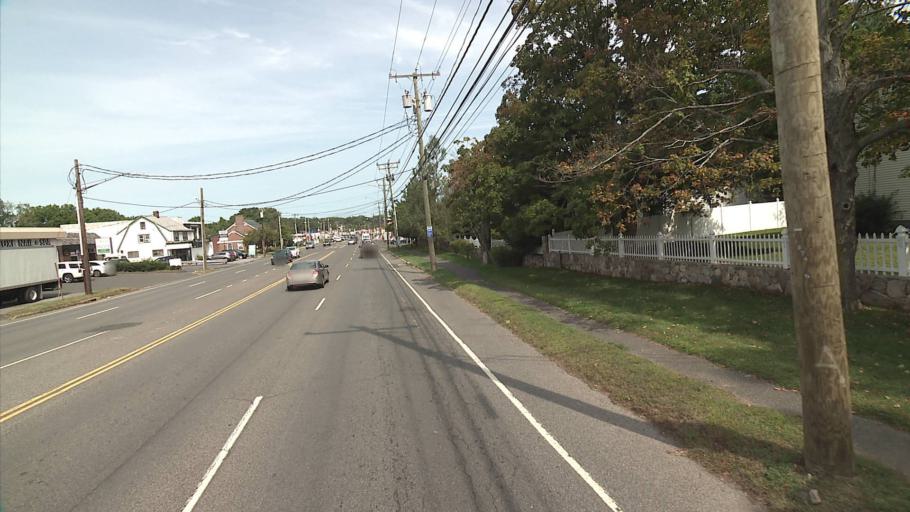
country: US
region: Connecticut
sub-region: Fairfield County
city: North Stamford
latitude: 41.1004
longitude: -73.5476
